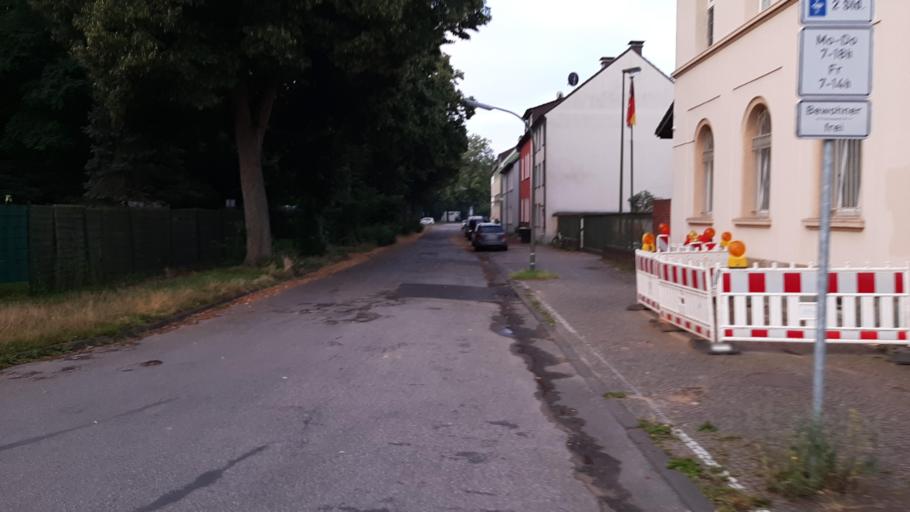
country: DE
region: North Rhine-Westphalia
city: Dorsten
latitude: 51.6718
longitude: 6.9733
